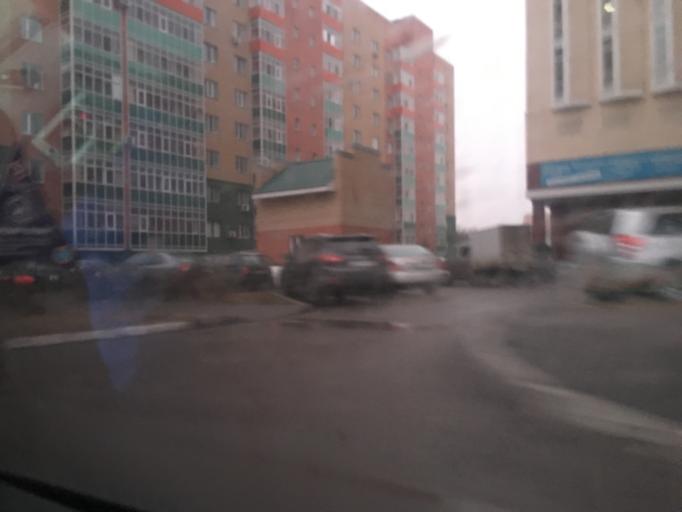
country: KZ
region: Astana Qalasy
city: Astana
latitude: 51.1610
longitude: 71.4356
